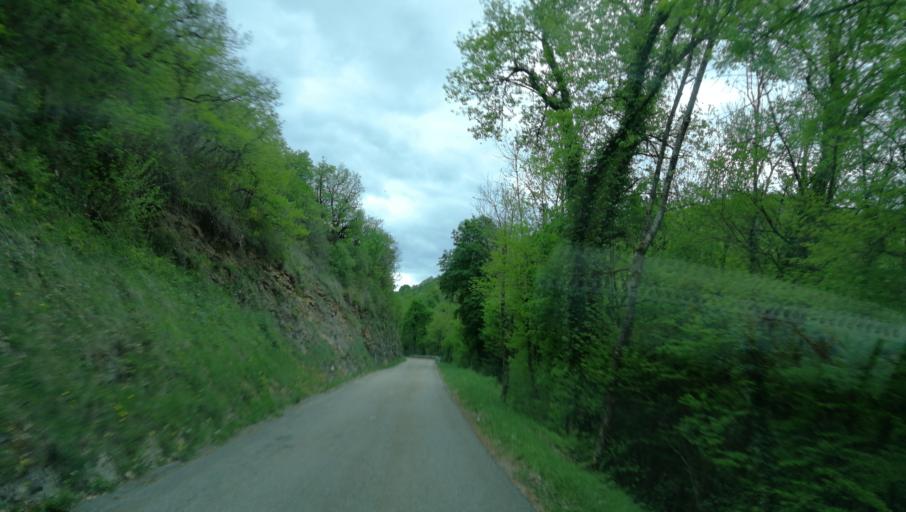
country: FR
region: Rhone-Alpes
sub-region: Departement de la Savoie
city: Chatillon
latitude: 45.7657
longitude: 5.8248
